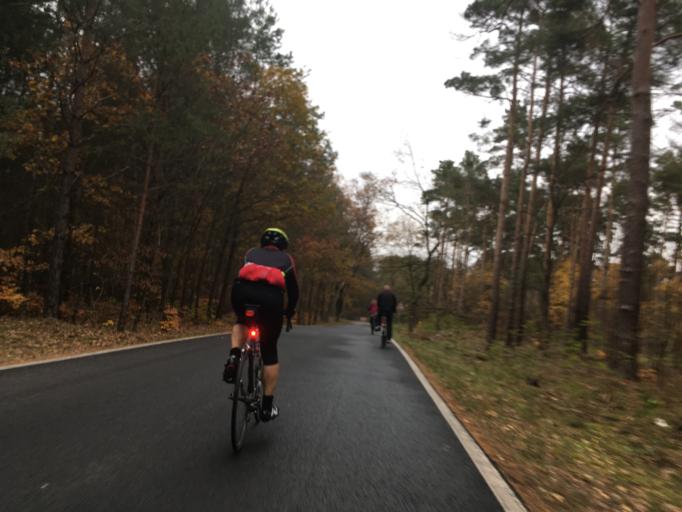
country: DE
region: Brandenburg
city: Gross Lindow
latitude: 52.2756
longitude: 14.4817
